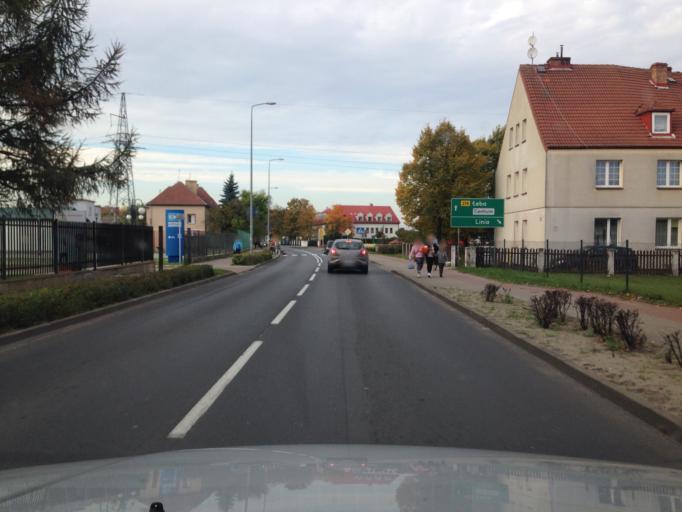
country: PL
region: Pomeranian Voivodeship
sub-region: Powiat leborski
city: Lebork
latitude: 54.5289
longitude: 17.7642
